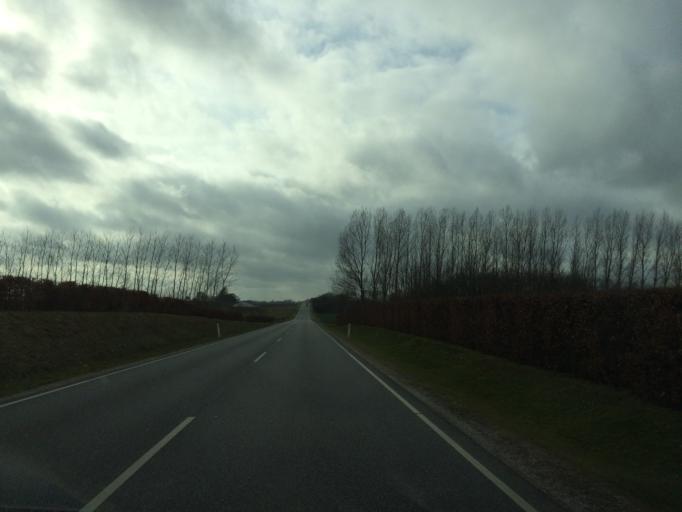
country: DK
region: Central Jutland
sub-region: Favrskov Kommune
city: Ulstrup
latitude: 56.4975
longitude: 9.8005
